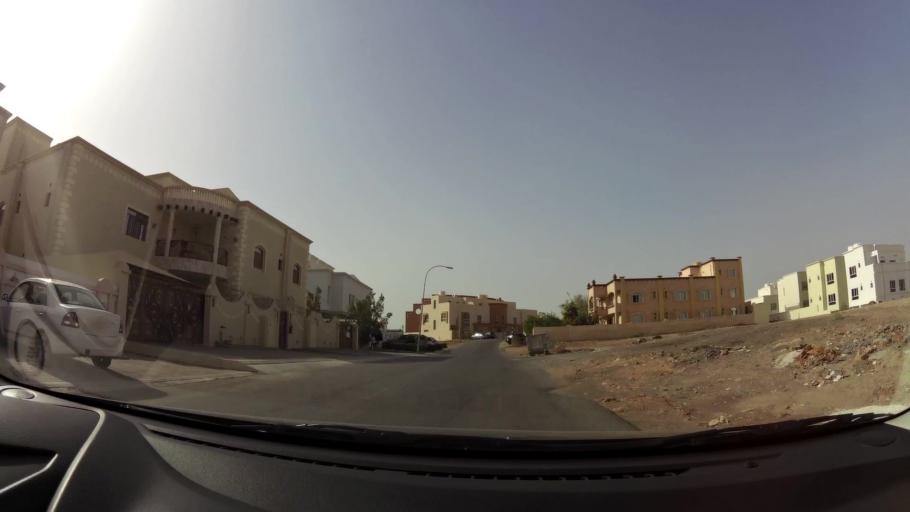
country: OM
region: Muhafazat Masqat
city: Bawshar
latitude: 23.5559
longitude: 58.3532
